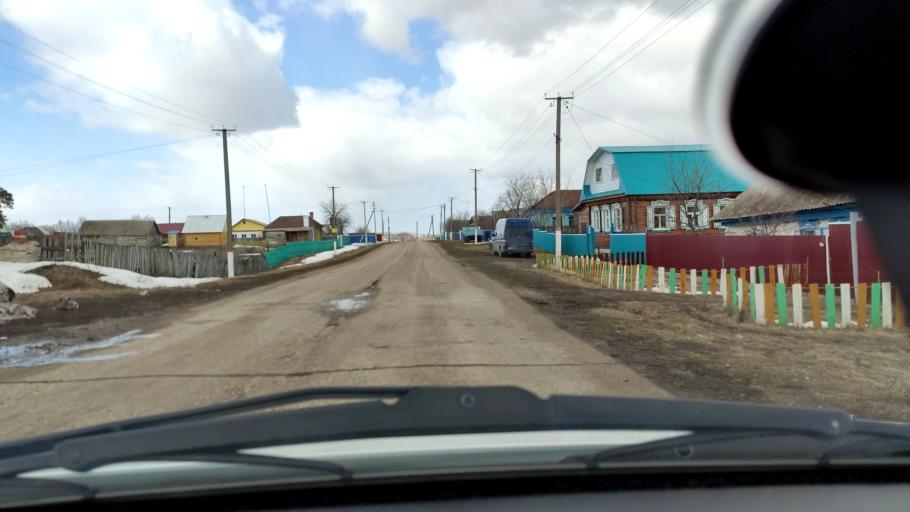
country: RU
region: Bashkortostan
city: Tolbazy
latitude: 54.1716
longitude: 55.9555
